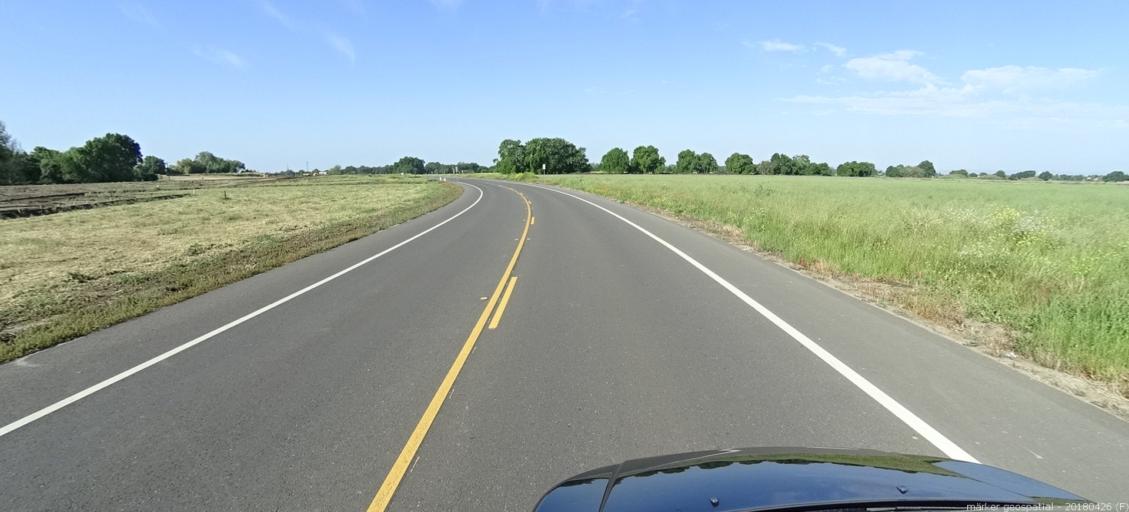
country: US
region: California
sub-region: Yolo County
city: West Sacramento
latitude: 38.5364
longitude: -121.5282
